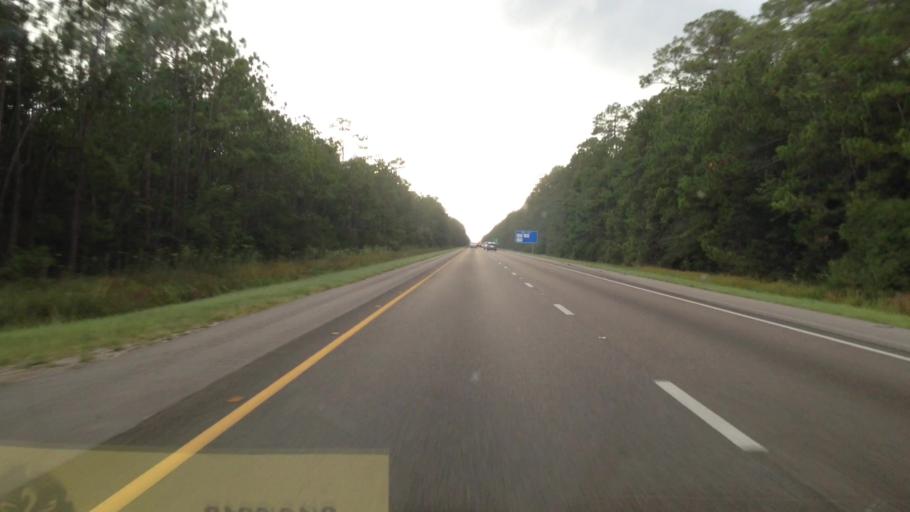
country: US
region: Mississippi
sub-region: Hancock County
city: Pearlington
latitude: 30.3246
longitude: -89.5704
